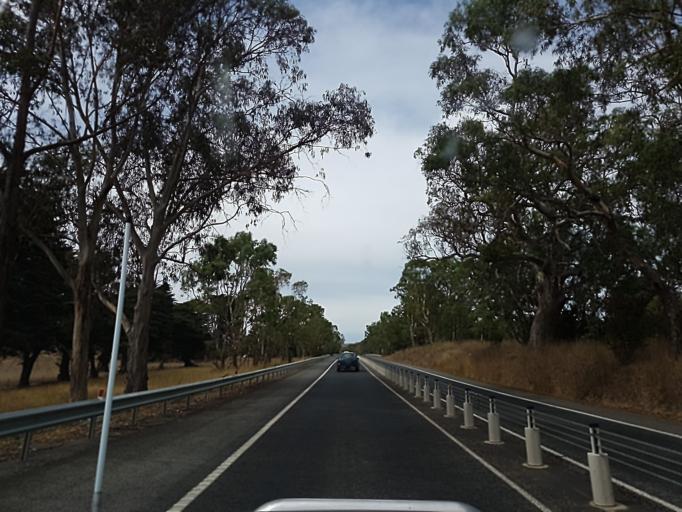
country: AU
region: Victoria
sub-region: Murrindindi
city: Alexandra
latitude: -37.2113
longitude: 145.4488
